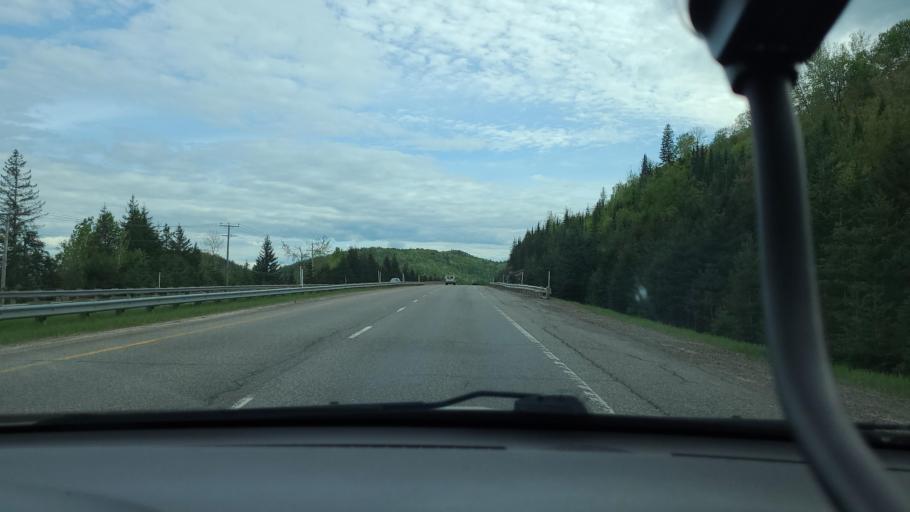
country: CA
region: Quebec
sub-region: Laurentides
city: Labelle
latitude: 46.2379
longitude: -74.7145
